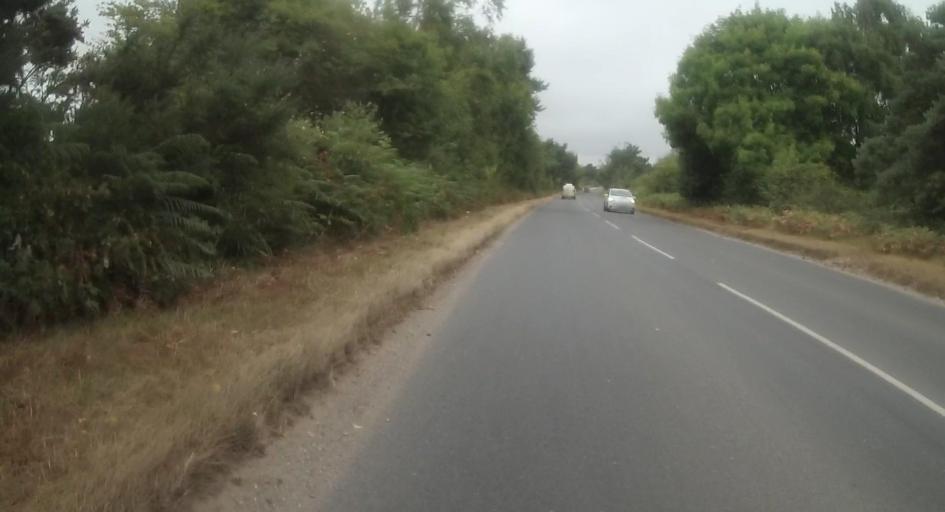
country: GB
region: England
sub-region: Dorset
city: Wool
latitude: 50.7002
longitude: -2.1936
